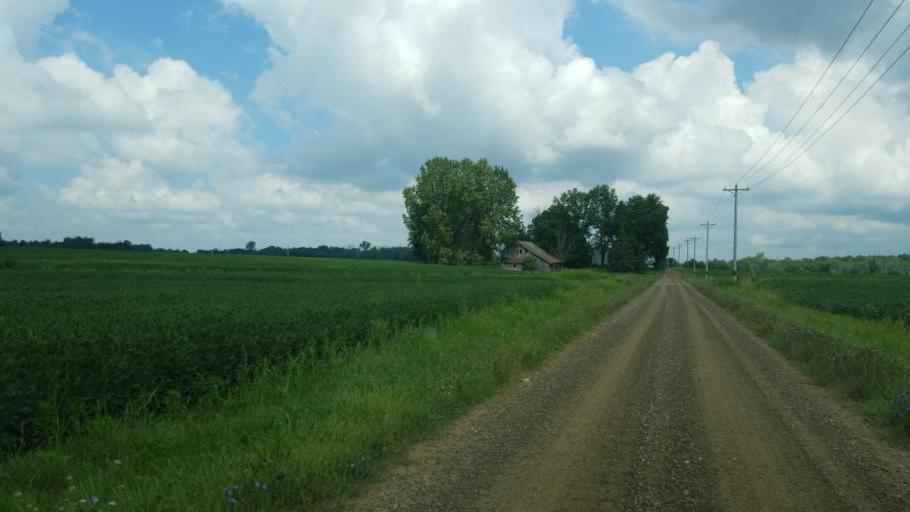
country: US
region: Ohio
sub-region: Knox County
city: Mount Vernon
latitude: 40.3298
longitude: -82.4867
